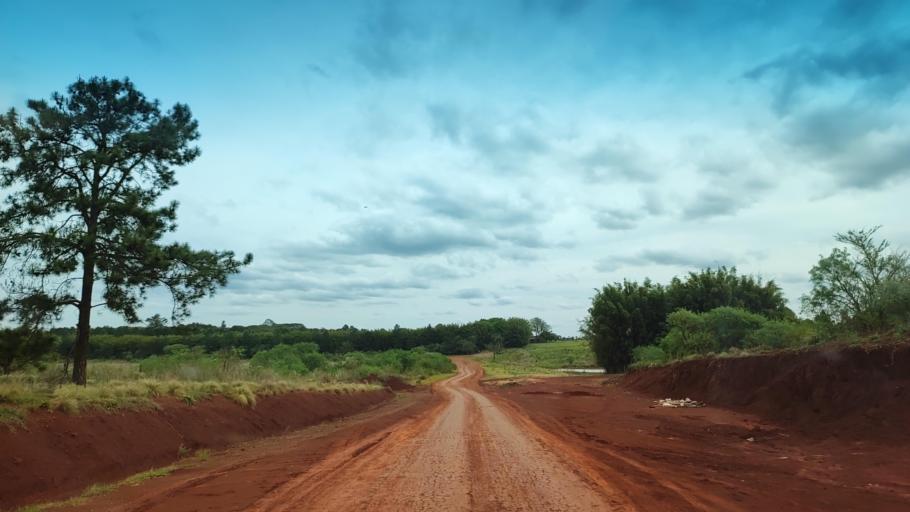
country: AR
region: Misiones
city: Garupa
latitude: -27.5156
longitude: -55.9719
